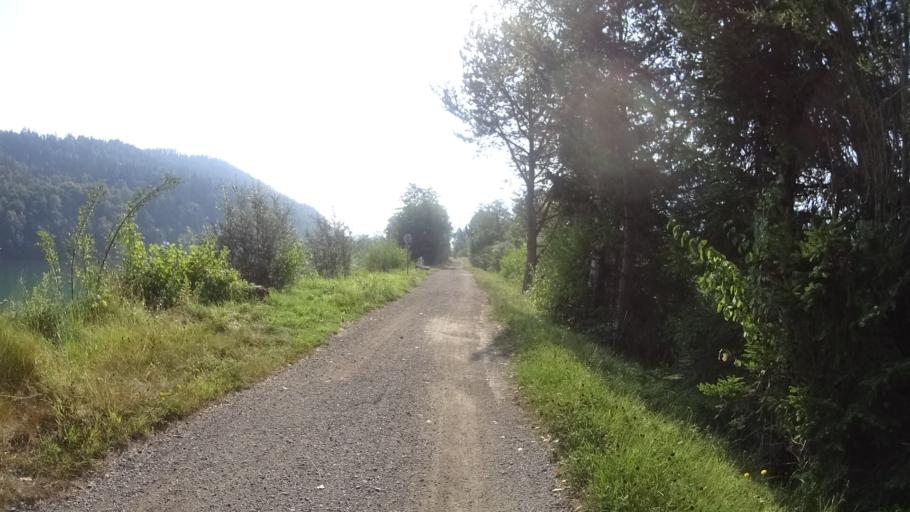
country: AT
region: Carinthia
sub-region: Politischer Bezirk Klagenfurt Land
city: Maria Rain
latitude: 46.5463
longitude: 14.2946
